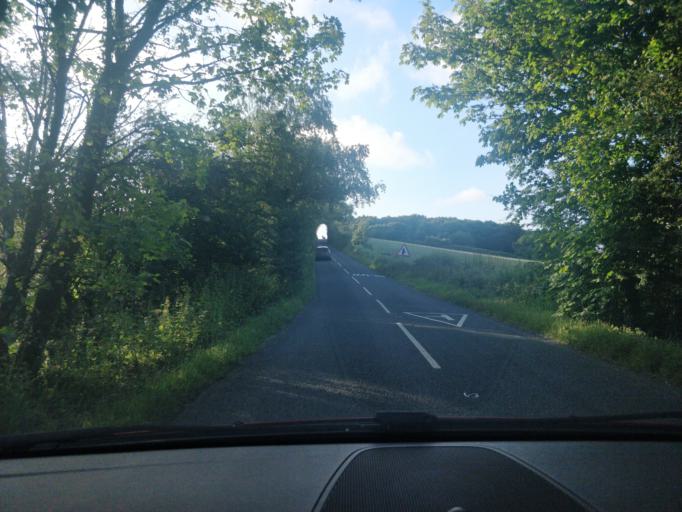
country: GB
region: England
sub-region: Lancashire
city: Skelmersdale
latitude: 53.5558
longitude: -2.7460
